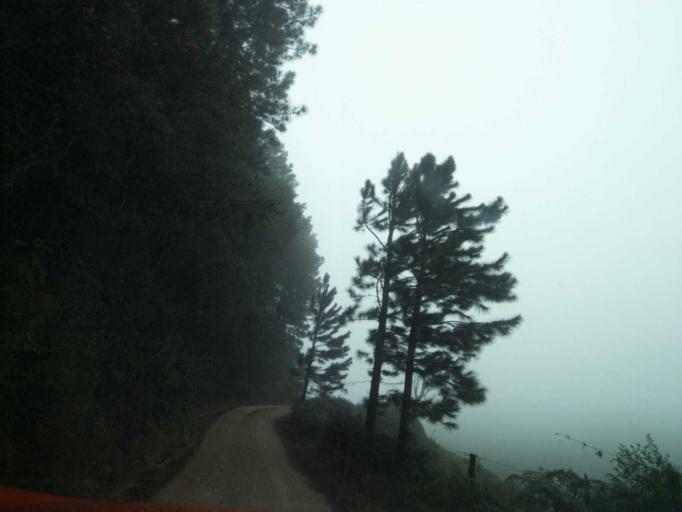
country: BR
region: Santa Catarina
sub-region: Anitapolis
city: Anitapolis
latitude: -27.9212
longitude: -49.2045
